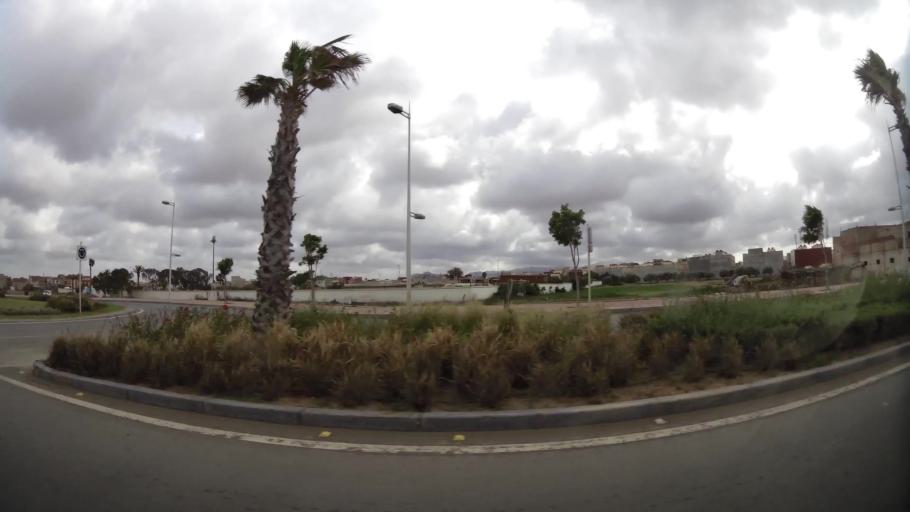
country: MA
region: Oriental
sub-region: Nador
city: Nador
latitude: 35.1630
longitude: -2.9097
